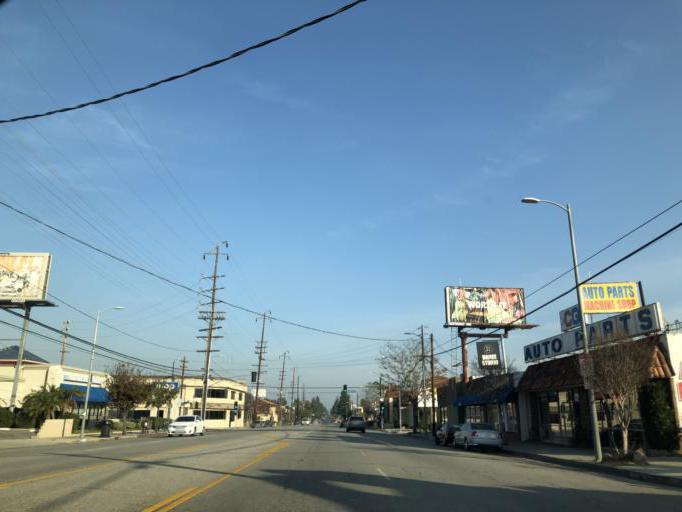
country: US
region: California
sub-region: Los Angeles County
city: Chatsworth
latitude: 34.2572
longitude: -118.5941
